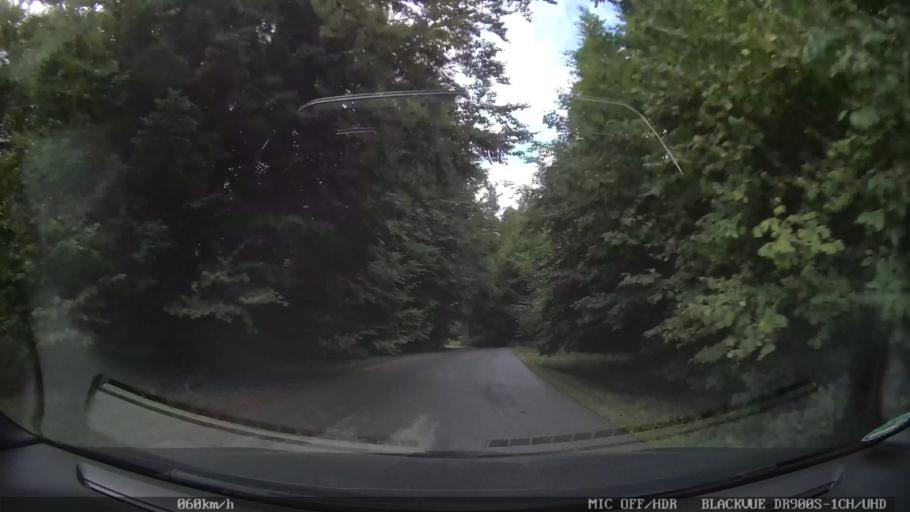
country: HR
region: Licko-Senjska
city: Jezerce
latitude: 44.9400
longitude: 15.5442
